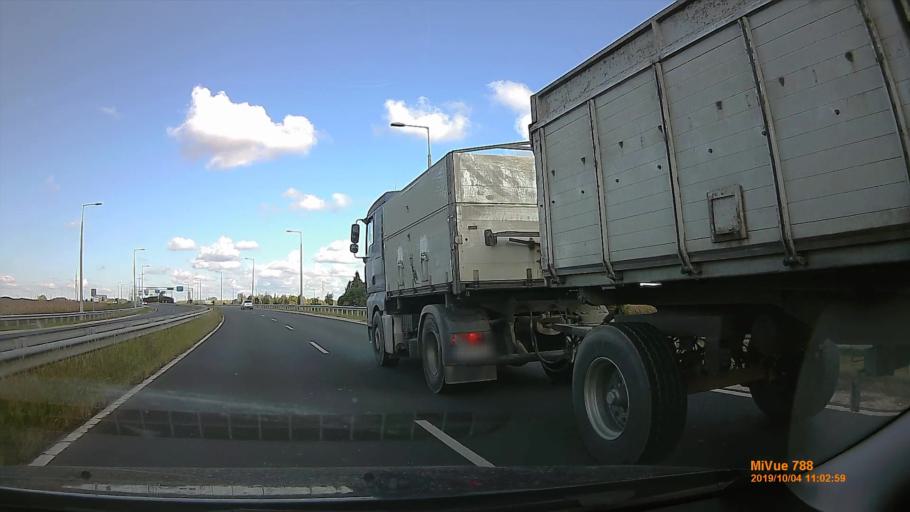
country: HU
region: Somogy
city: Kaposvar
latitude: 46.3931
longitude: 17.7787
